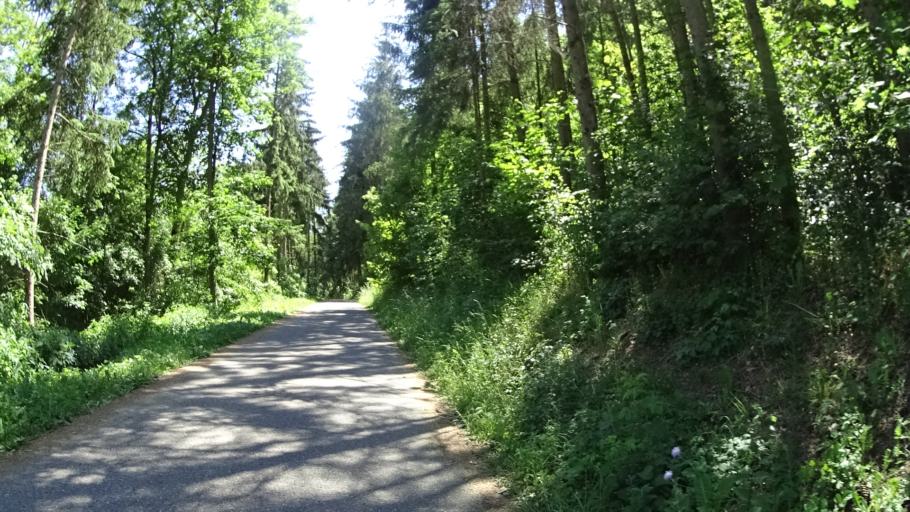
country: DE
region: Bavaria
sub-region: Regierungsbezirk Mittelfranken
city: Adelshofen
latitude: 49.4044
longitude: 10.1536
